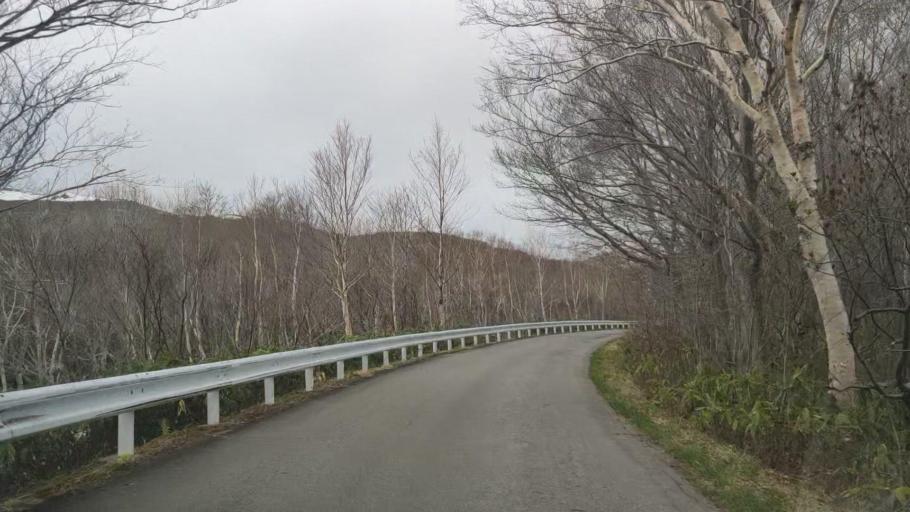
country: JP
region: Aomori
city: Aomori Shi
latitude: 40.6949
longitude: 140.9110
